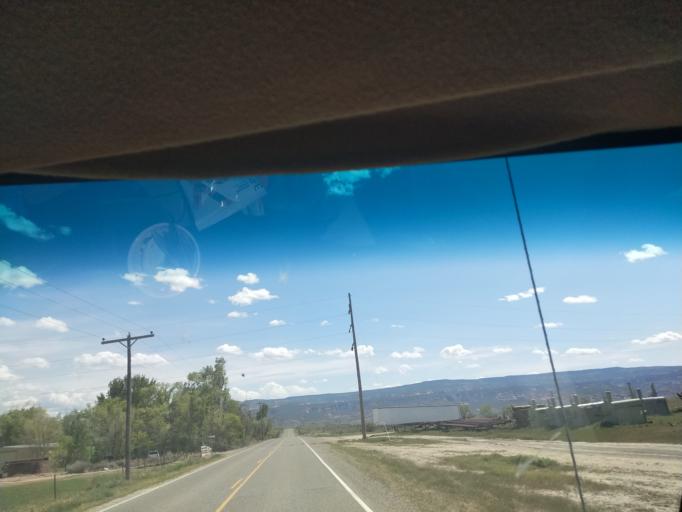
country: US
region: Colorado
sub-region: Mesa County
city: Fruita
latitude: 39.1985
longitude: -108.7570
